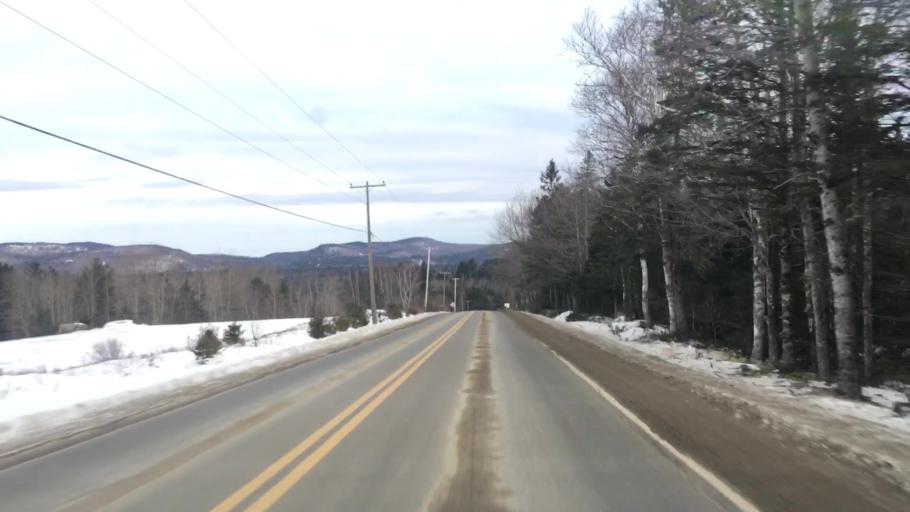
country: US
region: Maine
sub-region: Hancock County
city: Franklin
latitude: 44.8456
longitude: -68.3280
